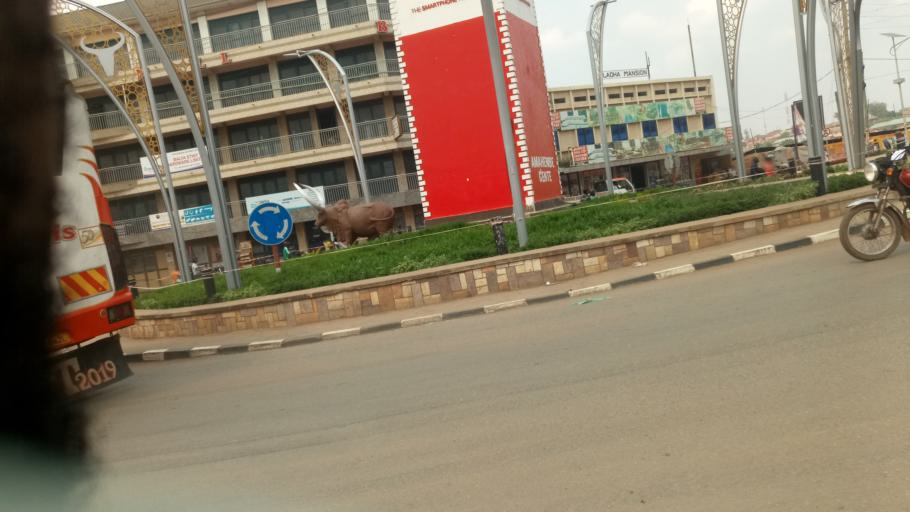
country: UG
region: Western Region
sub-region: Mbarara District
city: Mbarara
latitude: -0.6028
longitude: 30.6628
